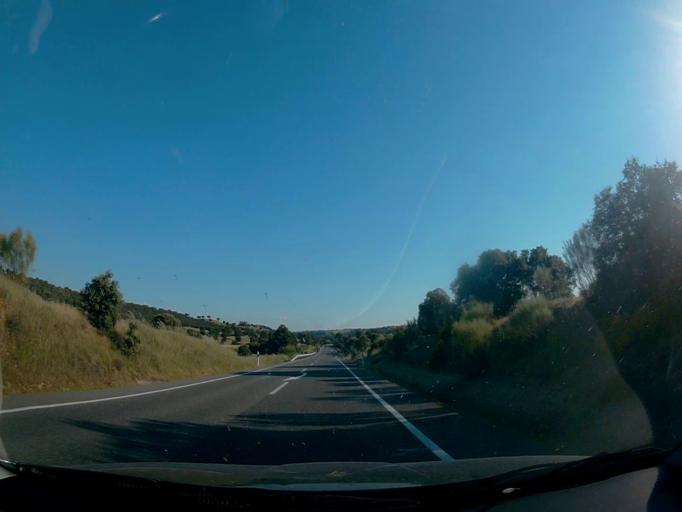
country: ES
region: Castille-La Mancha
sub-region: Province of Toledo
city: Almorox
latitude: 40.2027
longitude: -4.3979
